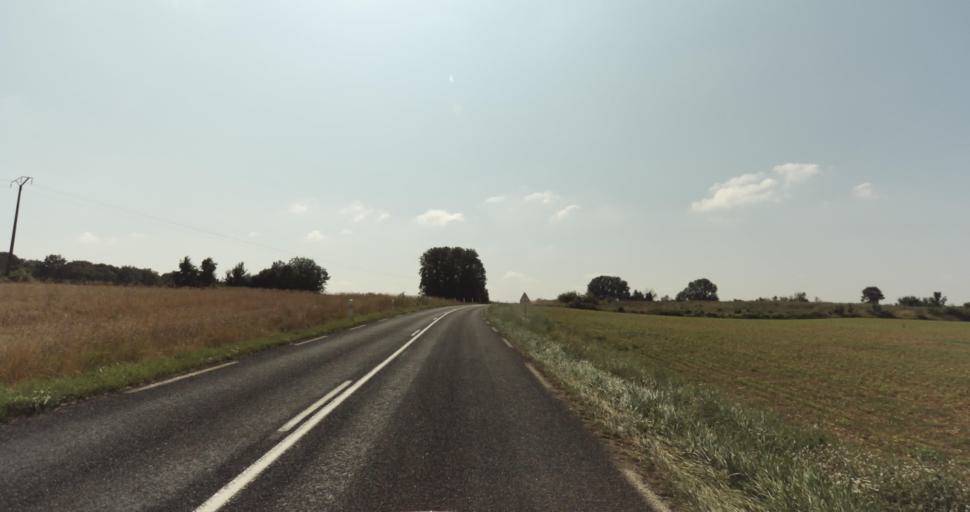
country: FR
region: Lorraine
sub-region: Departement de Meurthe-et-Moselle
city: Briey
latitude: 49.2579
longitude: 5.9197
